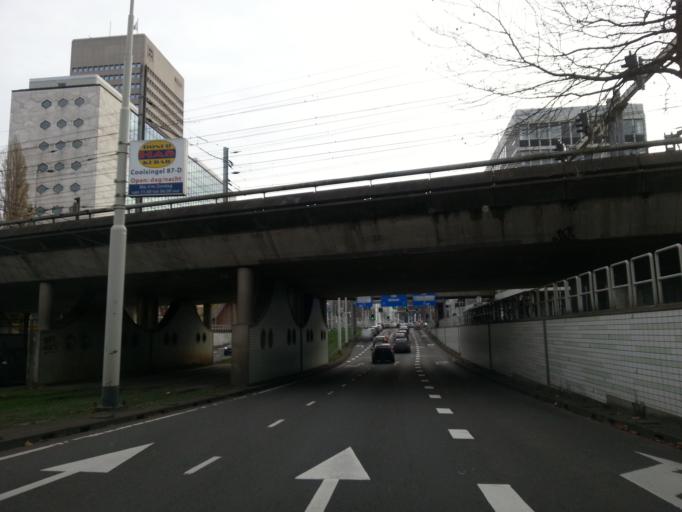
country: NL
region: South Holland
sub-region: Gemeente Rotterdam
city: Rotterdam
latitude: 51.9265
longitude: 4.4765
